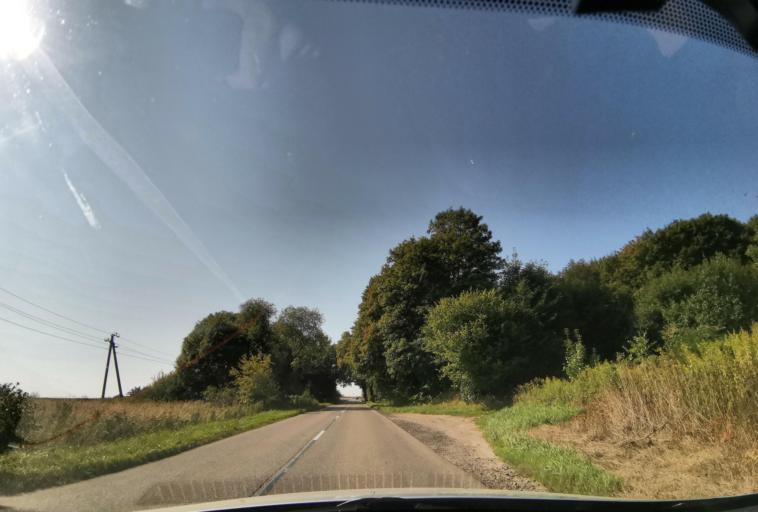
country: RU
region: Kaliningrad
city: Primorsk
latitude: 54.7943
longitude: 20.0360
